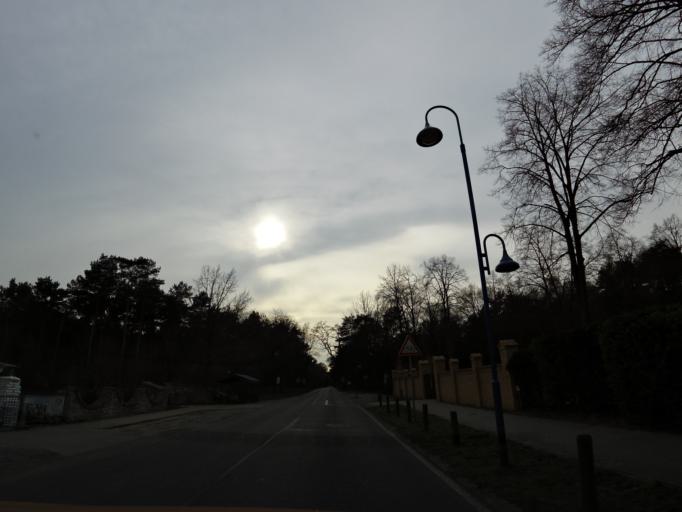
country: DE
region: Brandenburg
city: Bestensee
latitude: 52.2428
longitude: 13.6198
